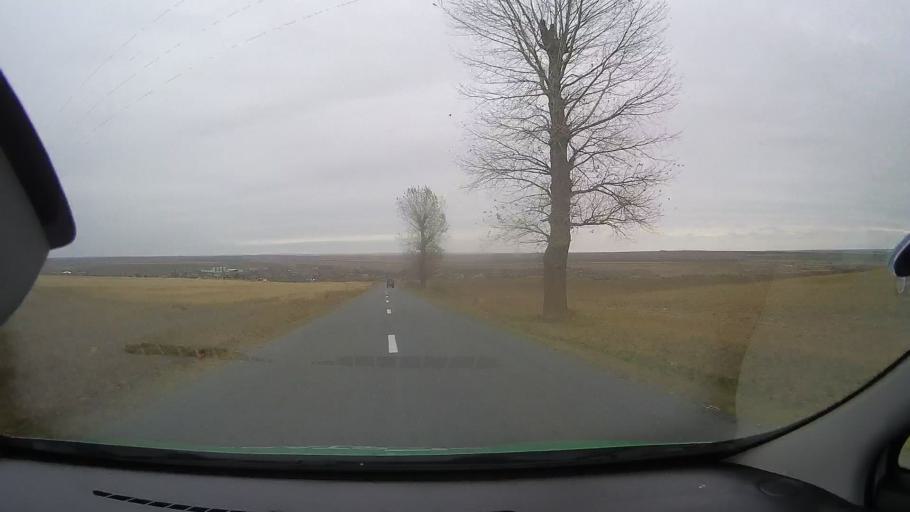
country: RO
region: Constanta
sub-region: Comuna Pantelimon
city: Pantelimon
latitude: 44.5923
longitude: 28.3214
